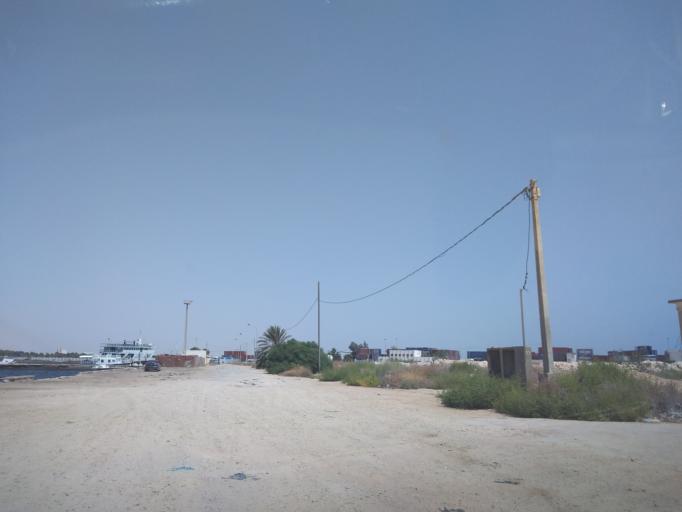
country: TN
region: Safaqis
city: Sfax
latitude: 34.7263
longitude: 10.7794
